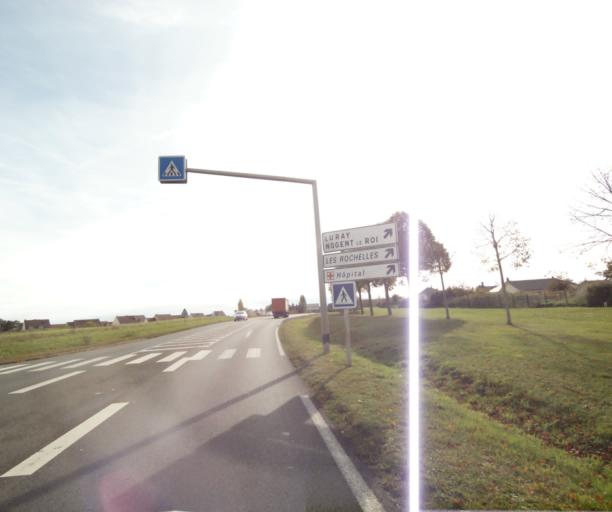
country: FR
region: Centre
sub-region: Departement d'Eure-et-Loir
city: Luray
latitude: 48.7315
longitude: 1.3897
